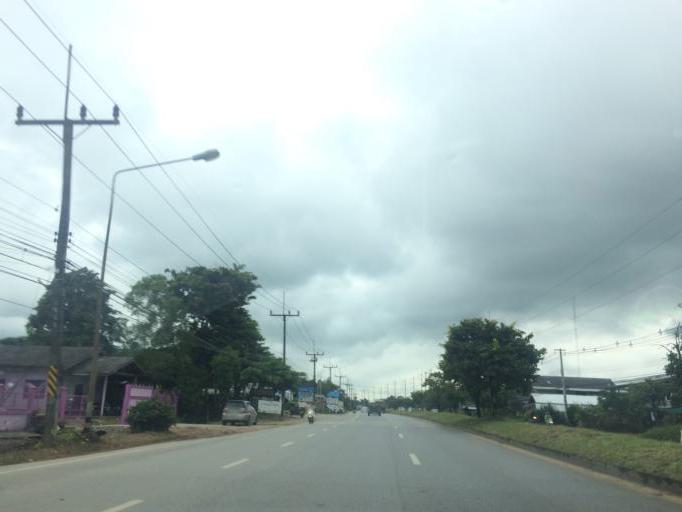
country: TH
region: Chiang Rai
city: Mae Chan
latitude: 20.0712
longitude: 99.8755
